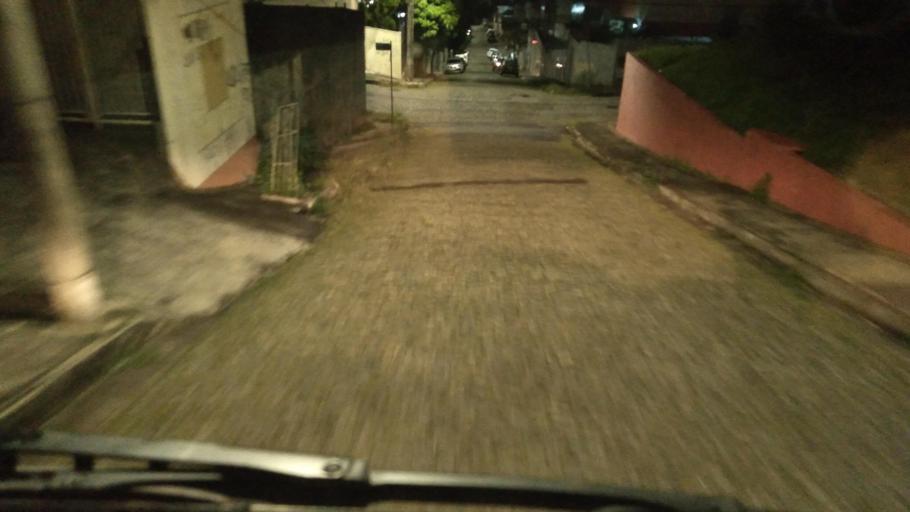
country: BR
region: Minas Gerais
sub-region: Belo Horizonte
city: Belo Horizonte
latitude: -19.9004
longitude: -43.9182
